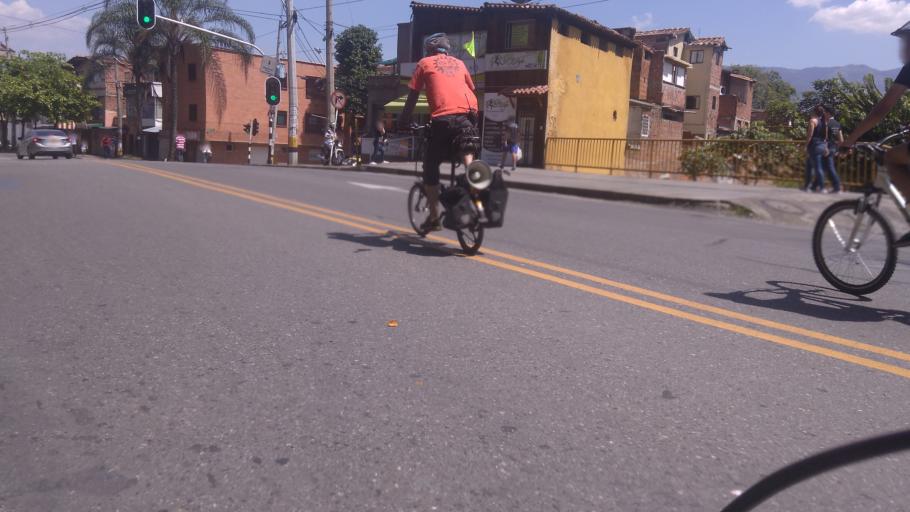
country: CO
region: Antioquia
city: Medellin
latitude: 6.2292
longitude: -75.5962
